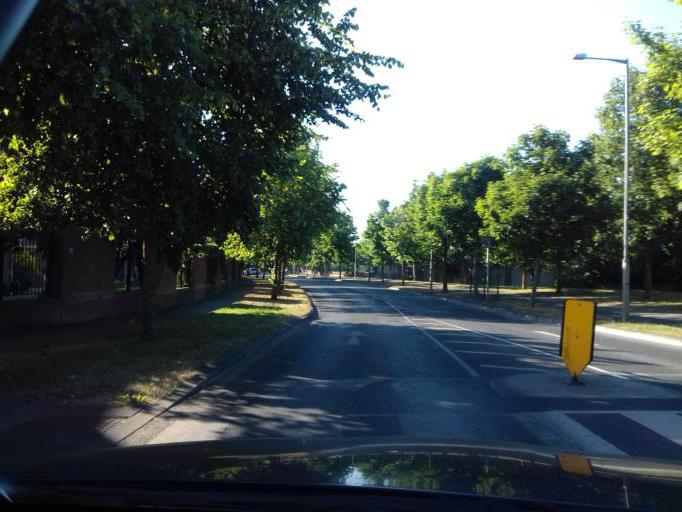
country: IE
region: Leinster
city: Hartstown
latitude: 53.3997
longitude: -6.4329
